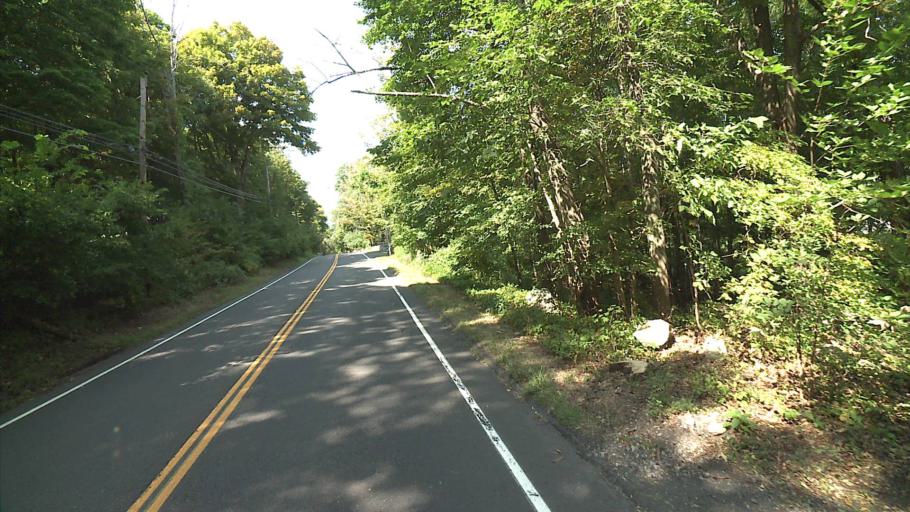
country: US
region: Connecticut
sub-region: Fairfield County
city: Georgetown
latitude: 41.2756
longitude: -73.3359
